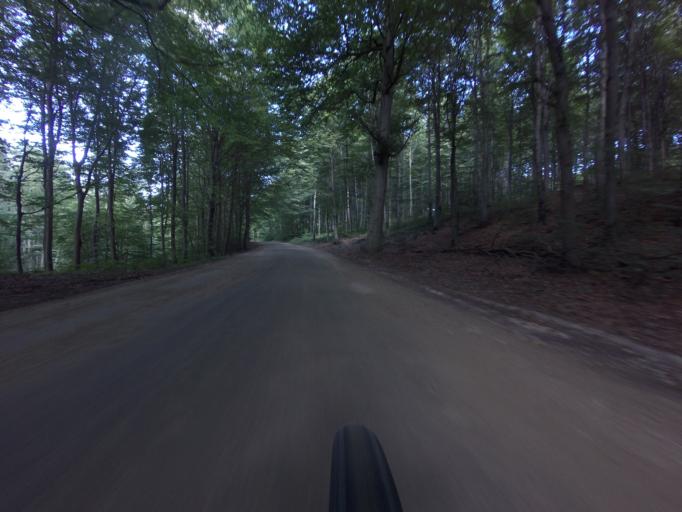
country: DK
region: Zealand
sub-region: Vordingborg Kommune
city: Stege
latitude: 54.9717
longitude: 12.5354
